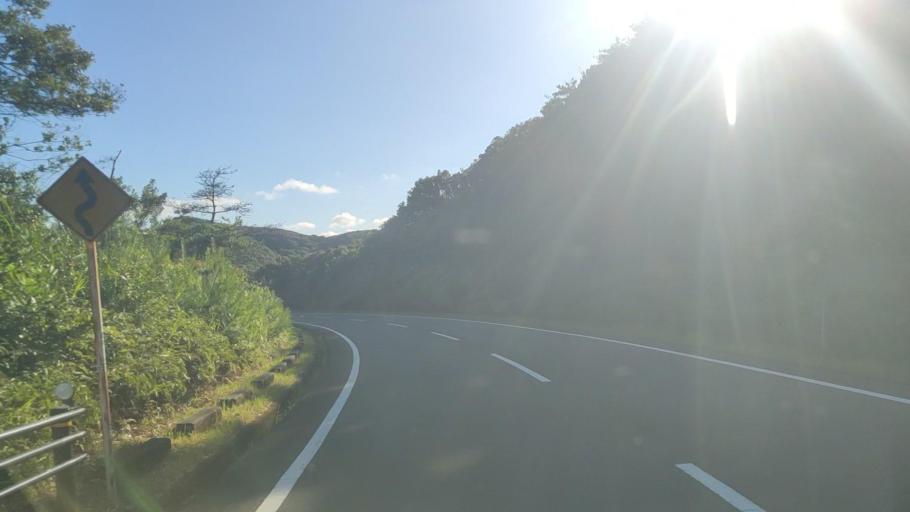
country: JP
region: Mie
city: Toba
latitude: 34.4158
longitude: 136.9089
